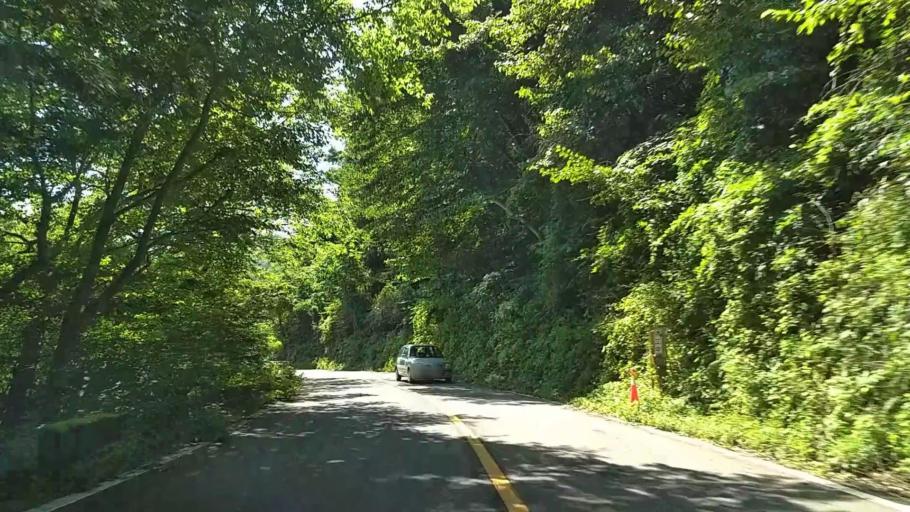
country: JP
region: Gunma
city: Annaka
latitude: 36.3540
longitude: 138.6842
